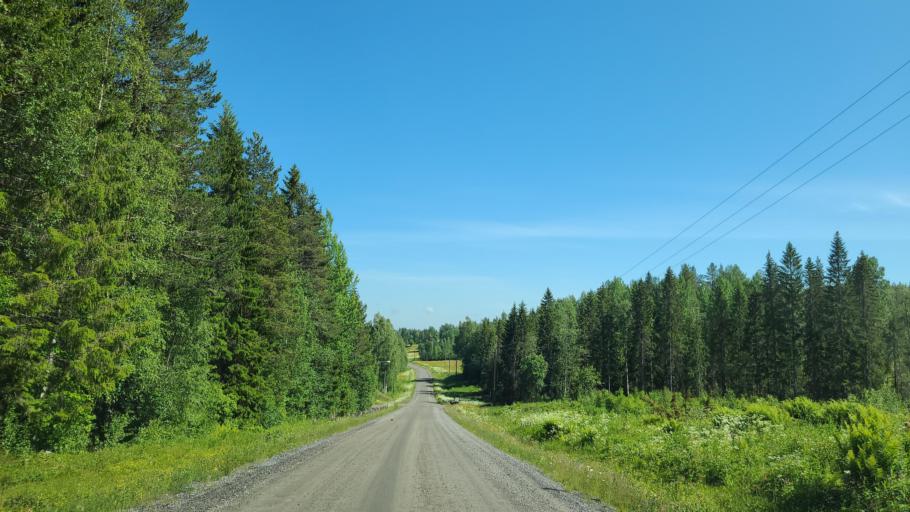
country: SE
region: Vaesterbotten
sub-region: Bjurholms Kommun
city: Bjurholm
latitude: 63.6424
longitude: 19.1671
